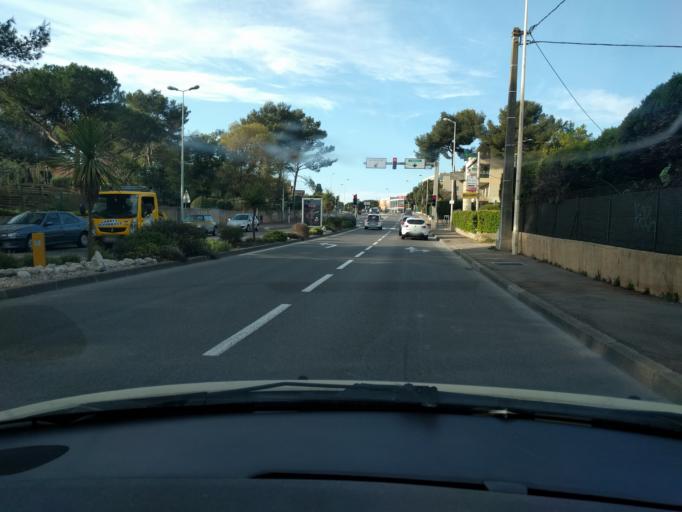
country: FR
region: Provence-Alpes-Cote d'Azur
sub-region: Departement des Alpes-Maritimes
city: Cannes
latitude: 43.5698
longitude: 6.9818
